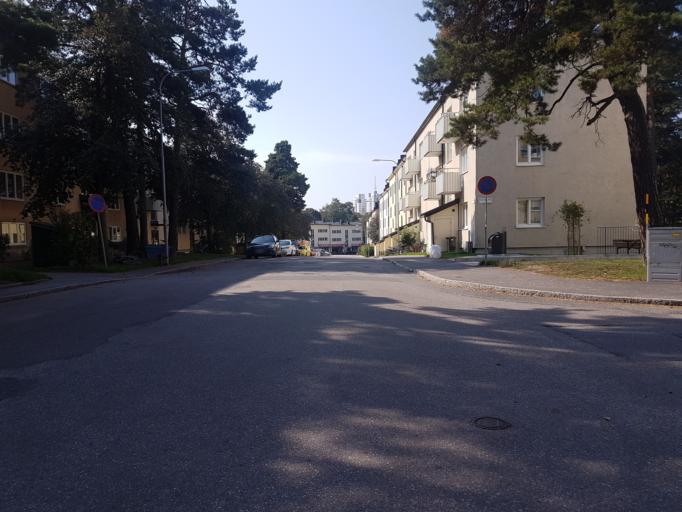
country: SE
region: Stockholm
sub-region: Stockholms Kommun
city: Arsta
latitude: 59.2994
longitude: 18.0907
